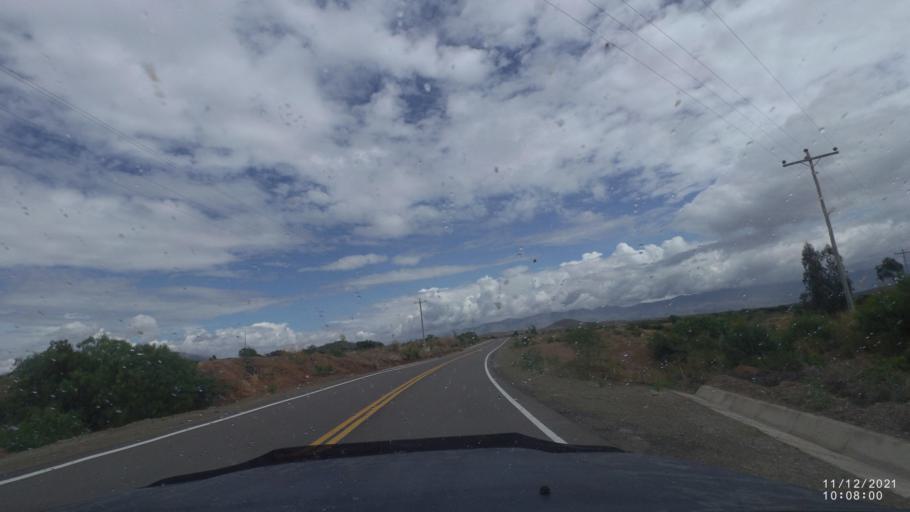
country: BO
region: Cochabamba
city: Tarata
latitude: -17.6736
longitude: -65.9606
